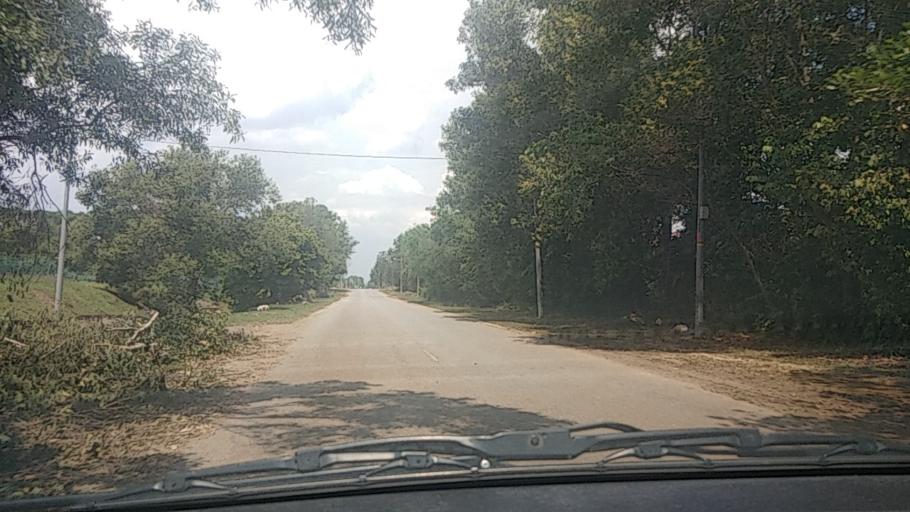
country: MY
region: Kedah
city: Sungai Petani
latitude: 5.6631
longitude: 100.5315
